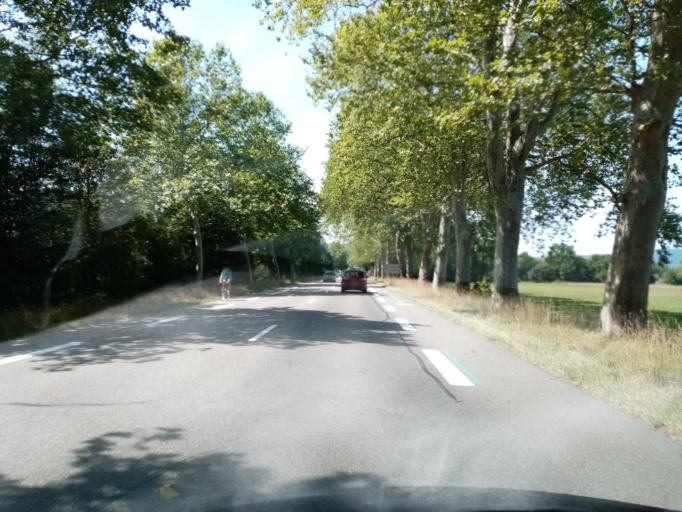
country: FR
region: Alsace
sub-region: Departement du Bas-Rhin
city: Selestat
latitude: 48.2442
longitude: 7.4657
